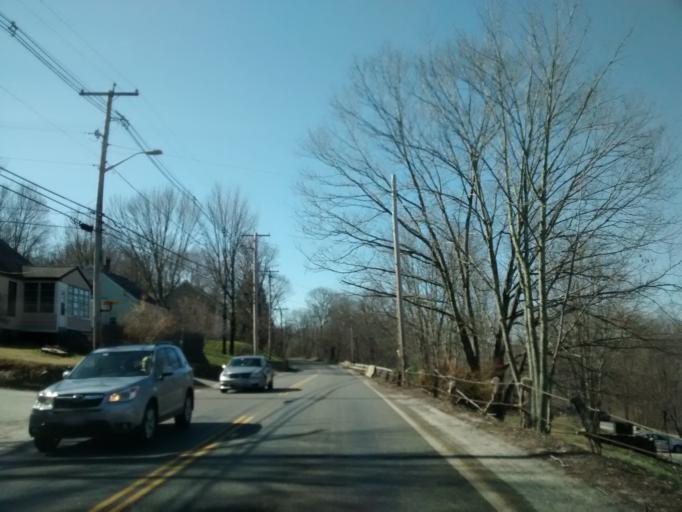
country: US
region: Massachusetts
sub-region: Worcester County
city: Northbridge
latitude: 42.1397
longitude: -71.6386
